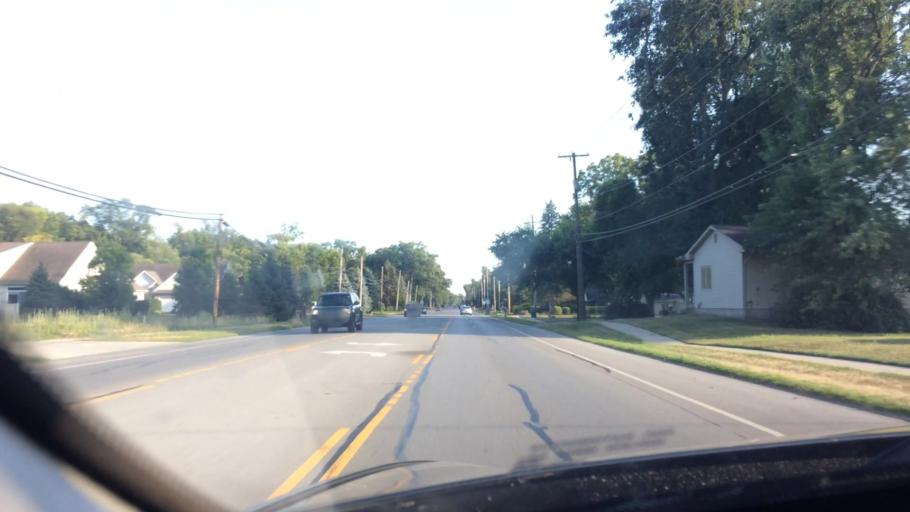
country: US
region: Ohio
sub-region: Lucas County
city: Sylvania
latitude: 41.6727
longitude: -83.7030
